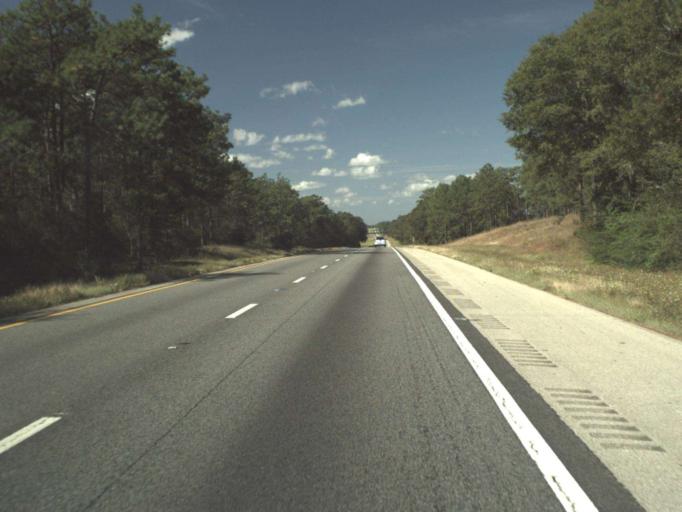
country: US
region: Florida
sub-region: Washington County
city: Chipley
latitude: 30.7461
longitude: -85.4885
